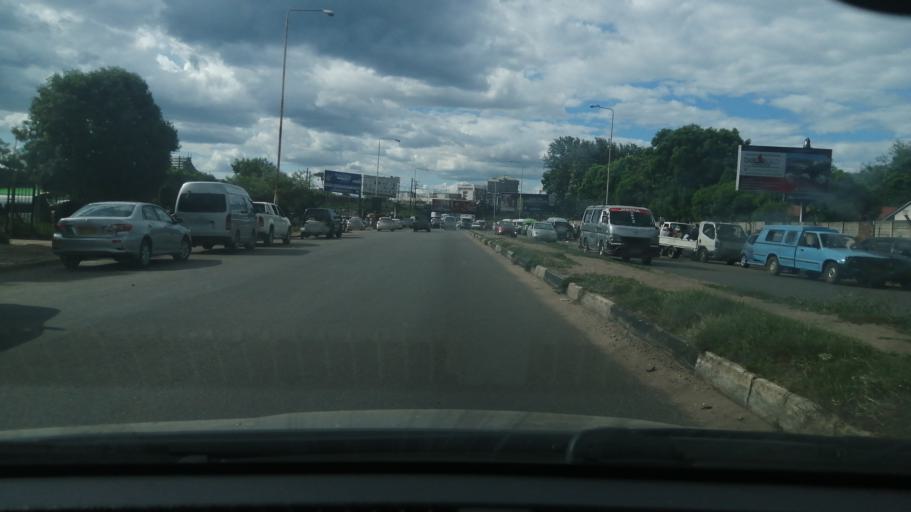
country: ZW
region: Harare
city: Harare
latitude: -17.8386
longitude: 31.0478
